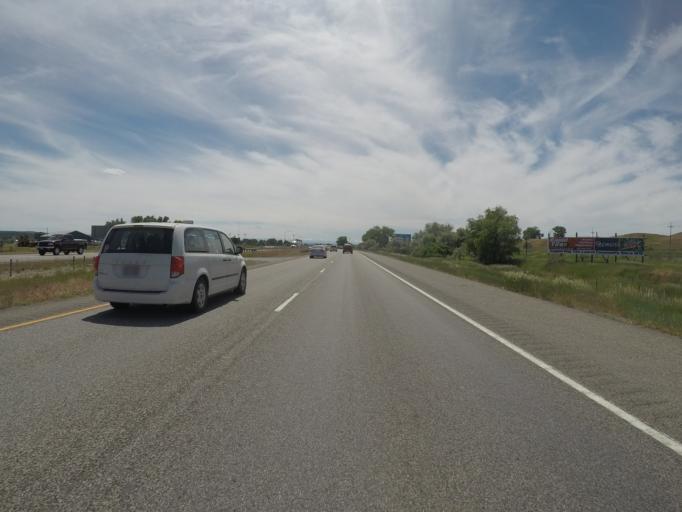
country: US
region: Montana
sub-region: Yellowstone County
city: Laurel
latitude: 45.6993
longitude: -108.6714
